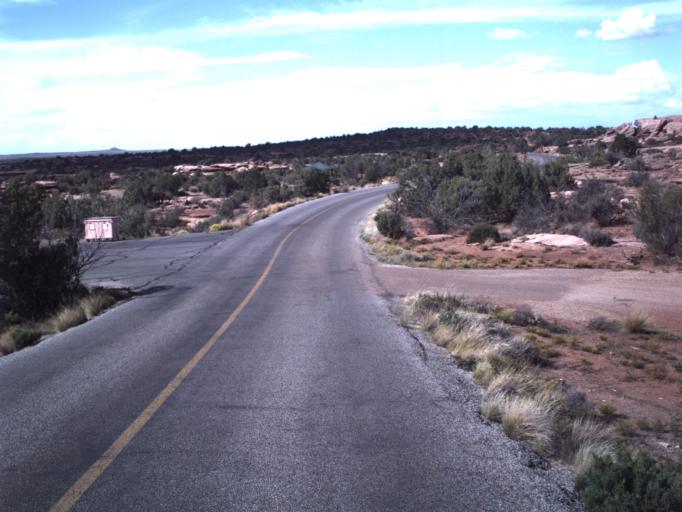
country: US
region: Utah
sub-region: Grand County
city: Moab
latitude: 38.4714
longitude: -109.7412
